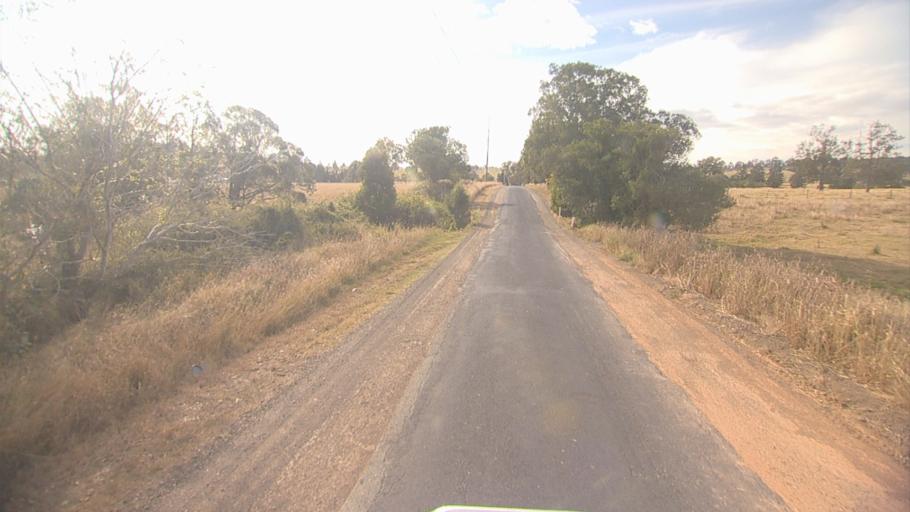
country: AU
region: Queensland
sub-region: Logan
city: Cedar Vale
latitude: -27.9180
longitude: 153.0132
